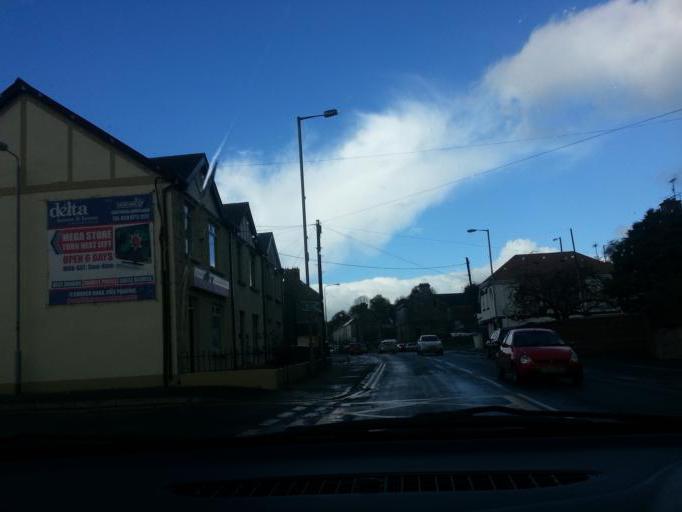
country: GB
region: Northern Ireland
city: Lisnaskea
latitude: 54.2502
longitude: -7.4415
